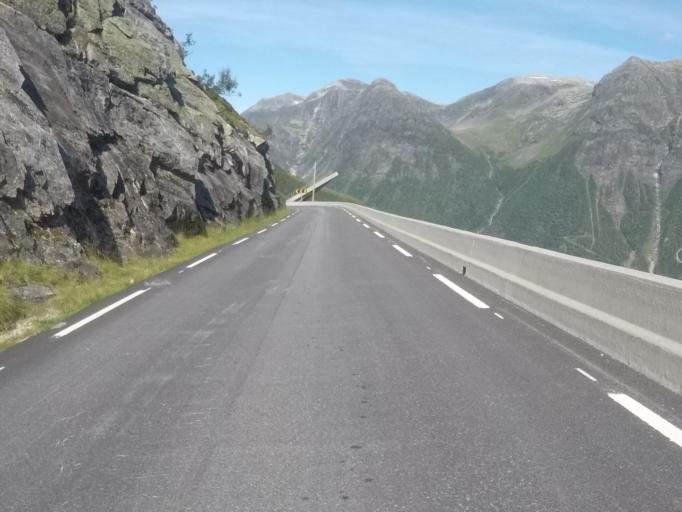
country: NO
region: Sogn og Fjordane
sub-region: Balestrand
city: Balestrand
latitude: 61.3505
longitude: 6.5172
